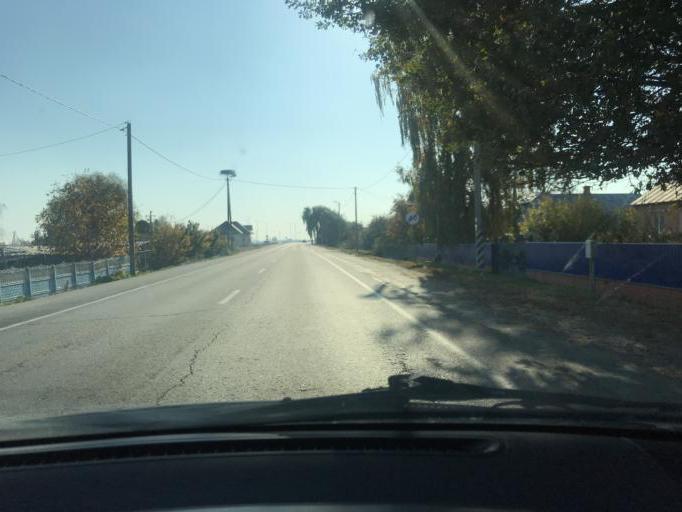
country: BY
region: Brest
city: Davyd-Haradok
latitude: 52.0710
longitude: 27.3383
